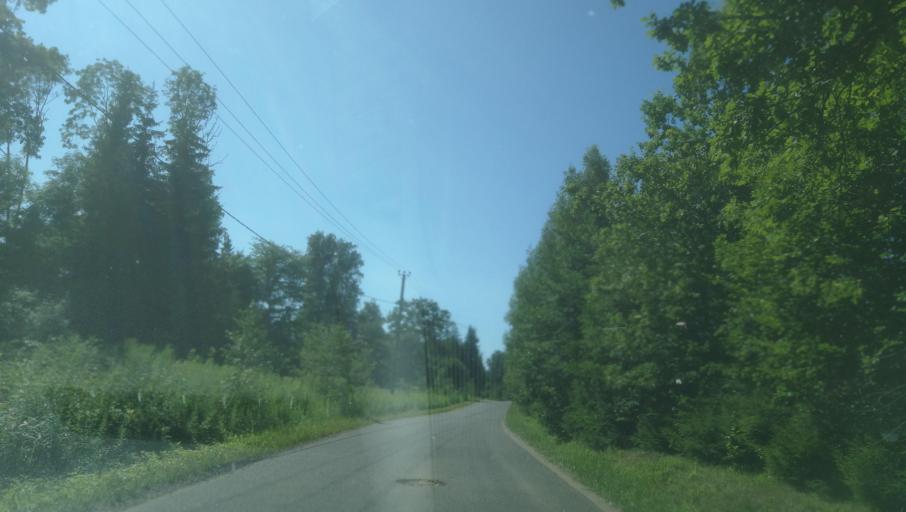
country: LV
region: Cesu Rajons
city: Cesis
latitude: 57.2879
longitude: 25.2253
